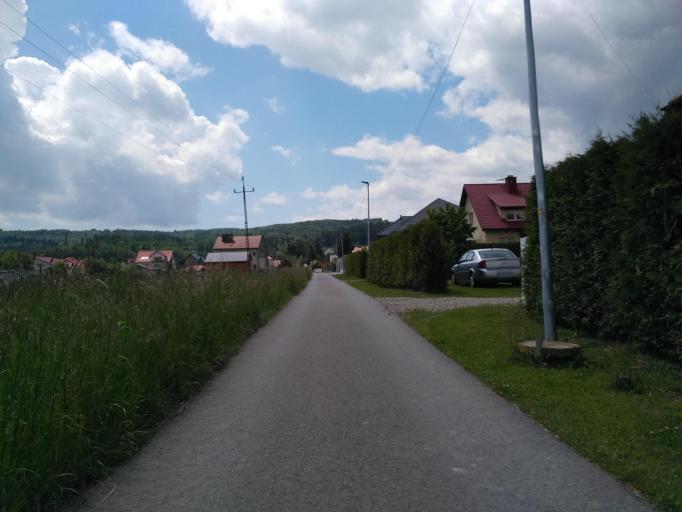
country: PL
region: Subcarpathian Voivodeship
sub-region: Powiat strzyzowski
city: Babica
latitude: 49.9303
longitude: 21.8531
